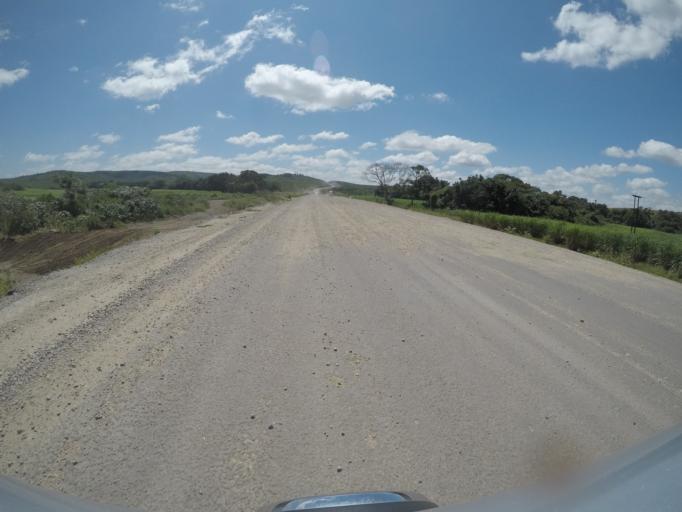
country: ZA
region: KwaZulu-Natal
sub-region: uThungulu District Municipality
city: Empangeni
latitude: -28.6476
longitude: 31.7678
